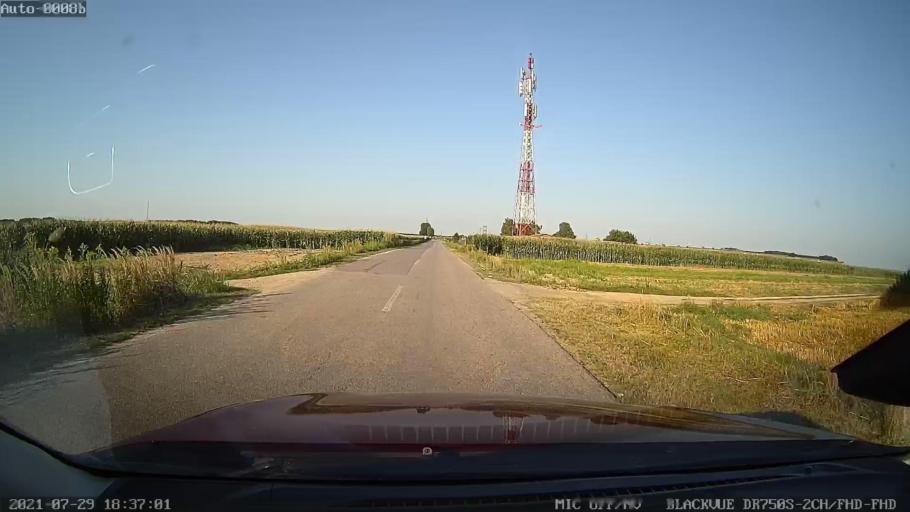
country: HR
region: Varazdinska
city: Petrijanec
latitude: 46.3198
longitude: 16.1937
